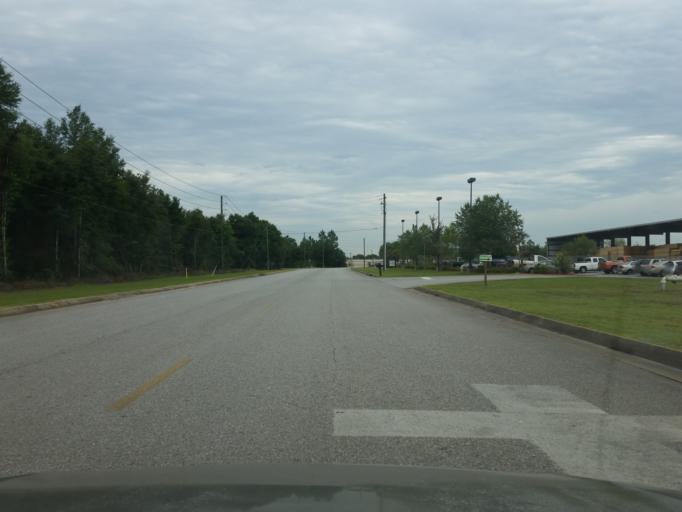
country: US
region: Florida
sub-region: Santa Rosa County
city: East Milton
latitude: 30.6386
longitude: -86.9735
